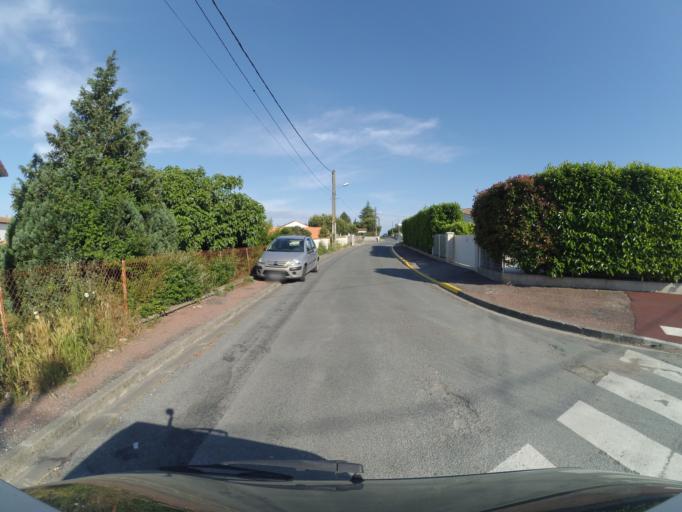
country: FR
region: Poitou-Charentes
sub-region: Departement de la Charente-Maritime
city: Royan
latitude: 45.6368
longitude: -1.0258
